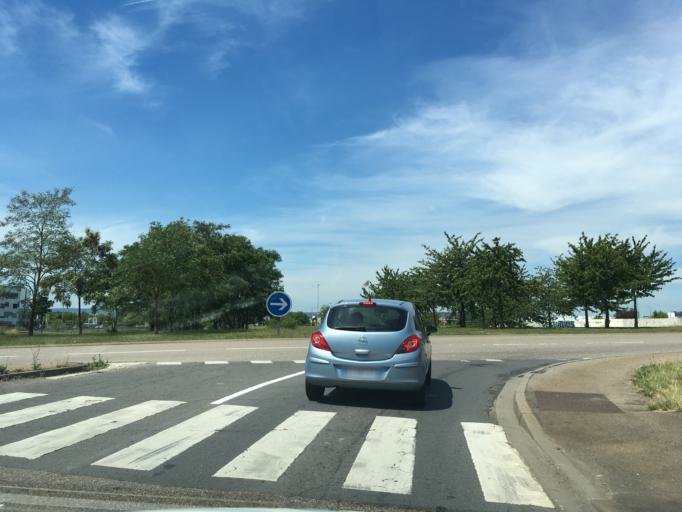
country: FR
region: Lorraine
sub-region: Departement de la Moselle
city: Peltre
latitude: 49.1078
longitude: 6.2371
